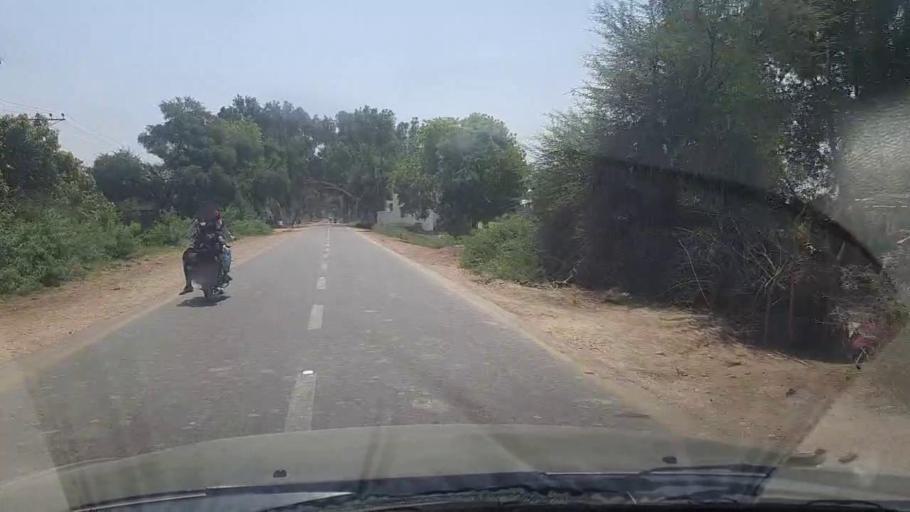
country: PK
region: Sindh
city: Tando Jam
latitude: 25.3520
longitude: 68.5071
